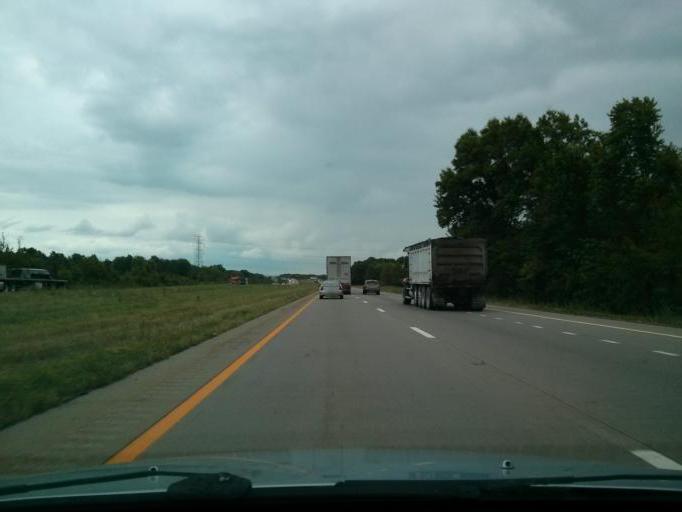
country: US
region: Ohio
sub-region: Trumbull County
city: Lordstown
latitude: 41.1069
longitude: -80.8803
